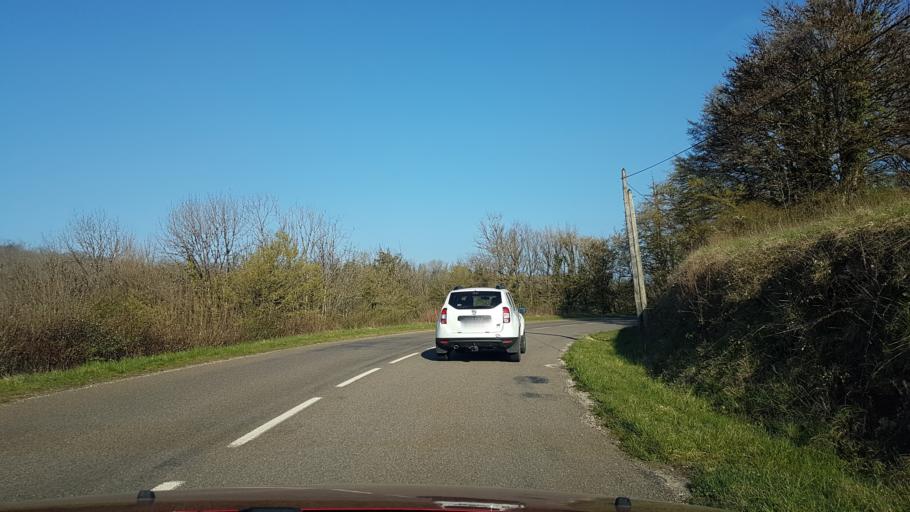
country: FR
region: Bourgogne
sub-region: Departement de Saone-et-Loire
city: Cuiseaux
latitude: 46.4496
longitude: 5.4186
